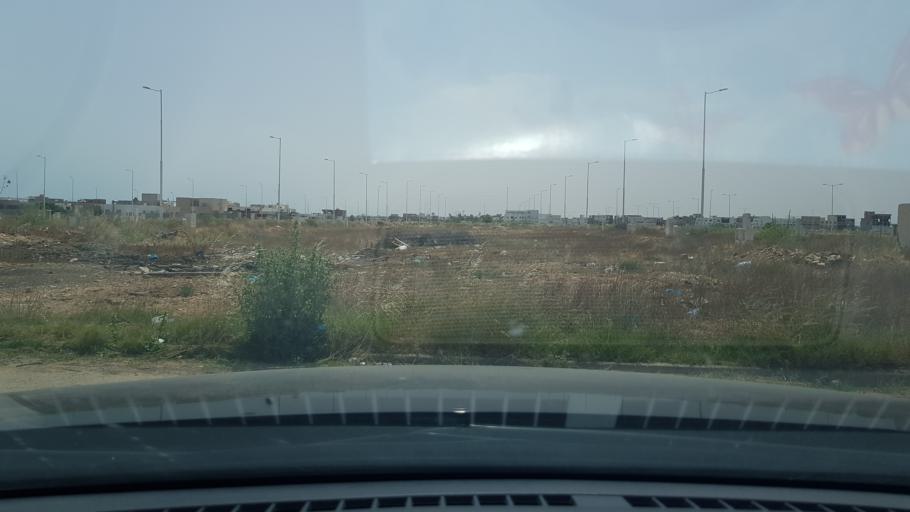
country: TN
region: Safaqis
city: Al Qarmadah
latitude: 34.8292
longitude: 10.7489
